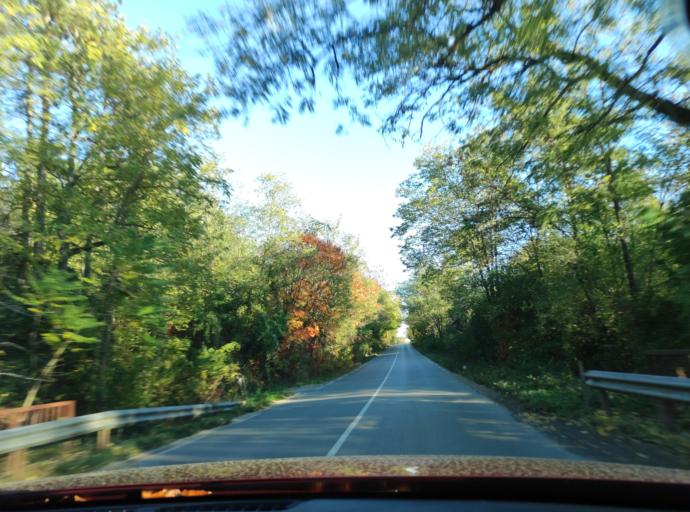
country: BG
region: Montana
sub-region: Obshtina Montana
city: Montana
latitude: 43.4001
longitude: 23.0926
